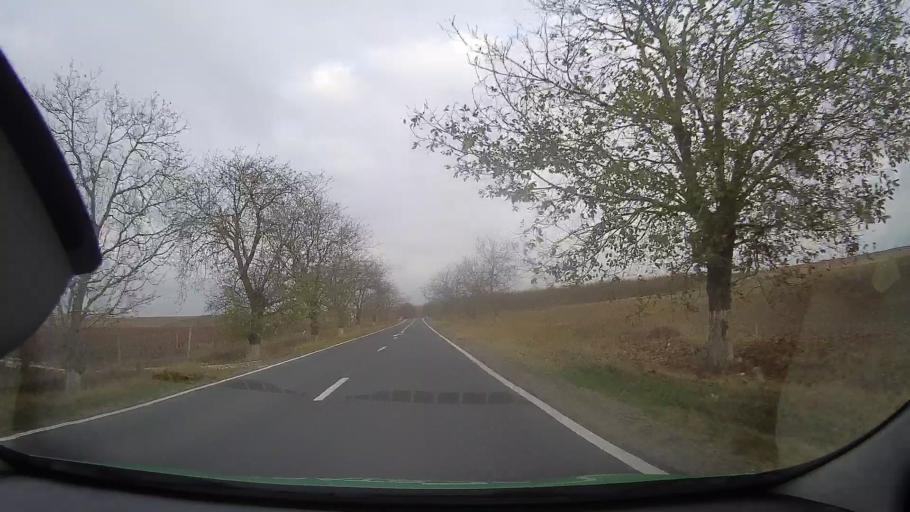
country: RO
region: Constanta
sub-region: Comuna Adamclisi
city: Adamclisi
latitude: 44.0881
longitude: 27.9707
